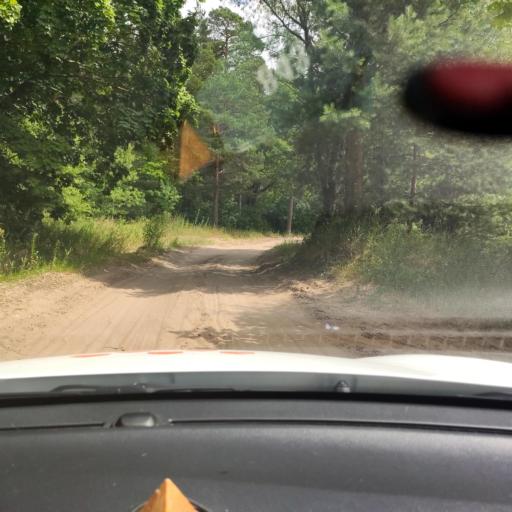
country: RU
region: Tatarstan
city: Osinovo
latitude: 55.9114
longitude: 48.9619
